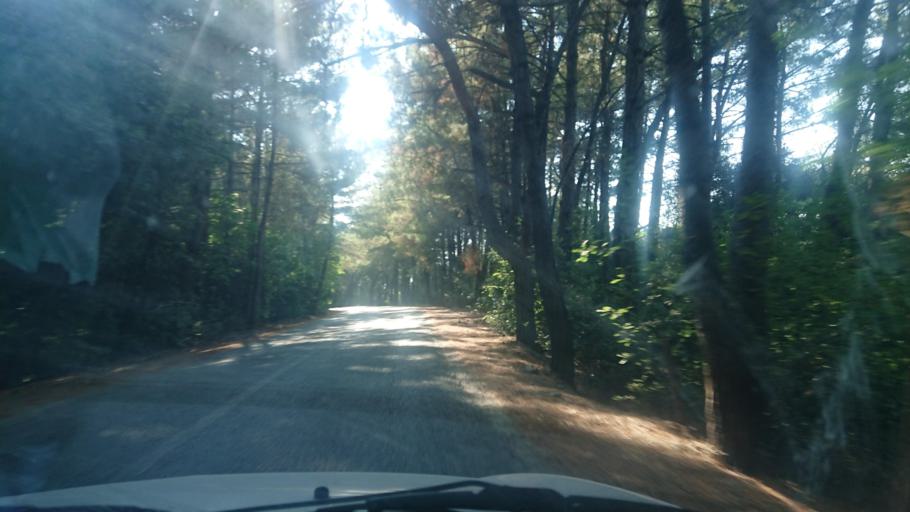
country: TR
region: Aydin
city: Atburgazi
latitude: 37.6898
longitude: 27.1370
